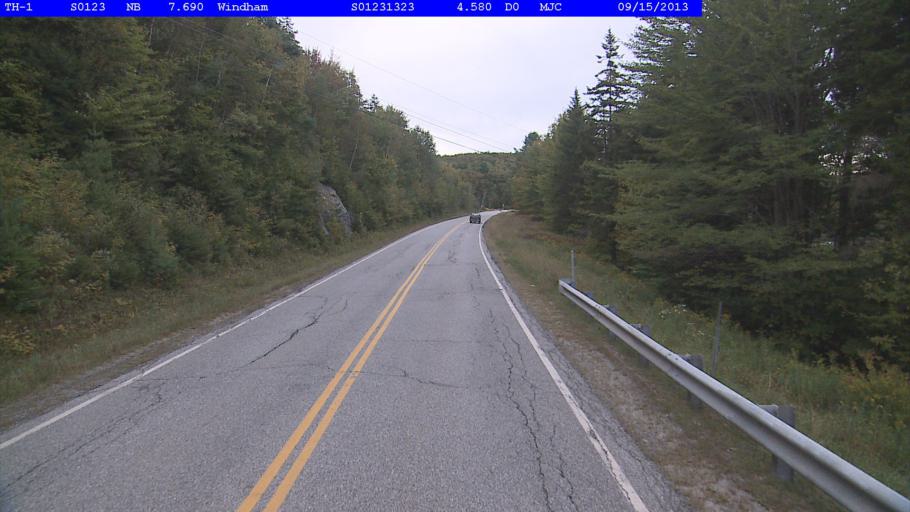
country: US
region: Vermont
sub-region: Windsor County
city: Chester
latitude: 43.1893
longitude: -72.7216
